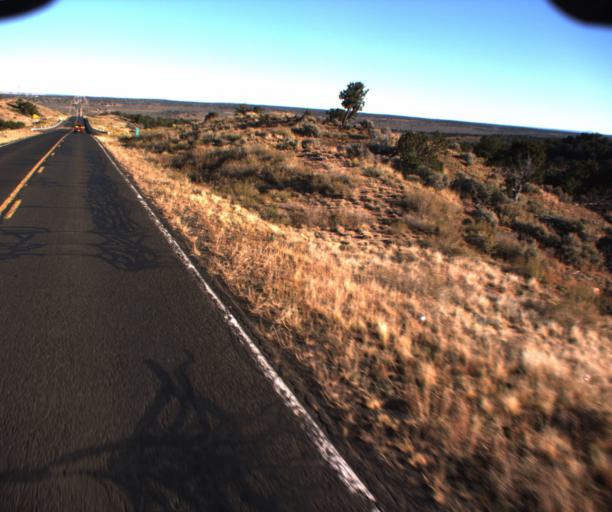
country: US
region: Arizona
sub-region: Apache County
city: Ganado
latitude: 35.5844
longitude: -109.5369
